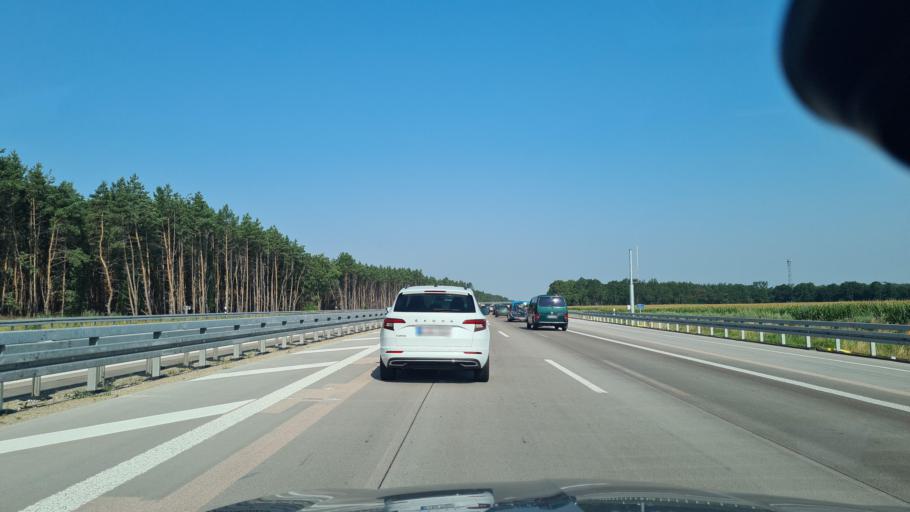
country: DE
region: Brandenburg
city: Kremmen
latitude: 52.7238
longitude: 12.9430
